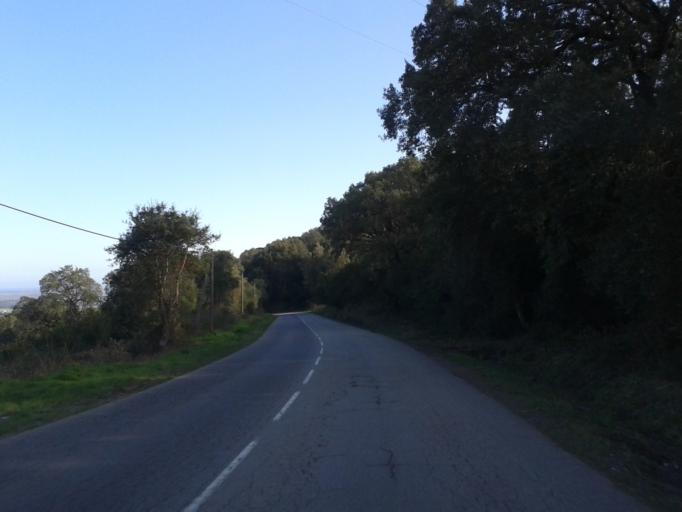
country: FR
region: Corsica
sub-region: Departement de la Haute-Corse
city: Biguglia
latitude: 42.5970
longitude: 9.4227
